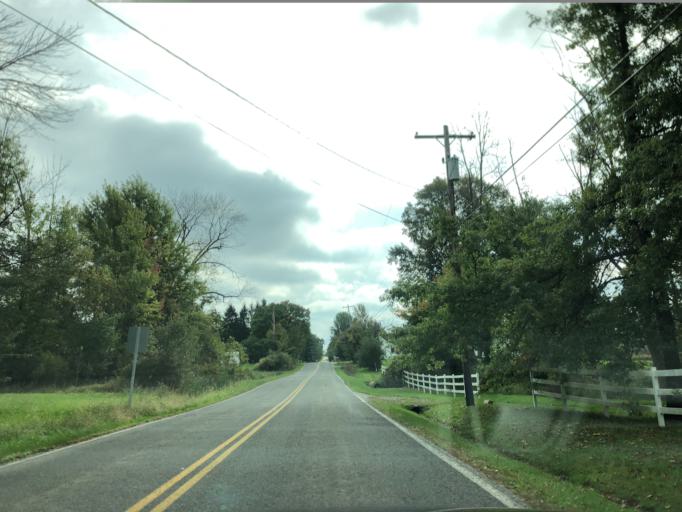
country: US
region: Ohio
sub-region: Summit County
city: Boston Heights
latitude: 41.2699
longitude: -81.5216
